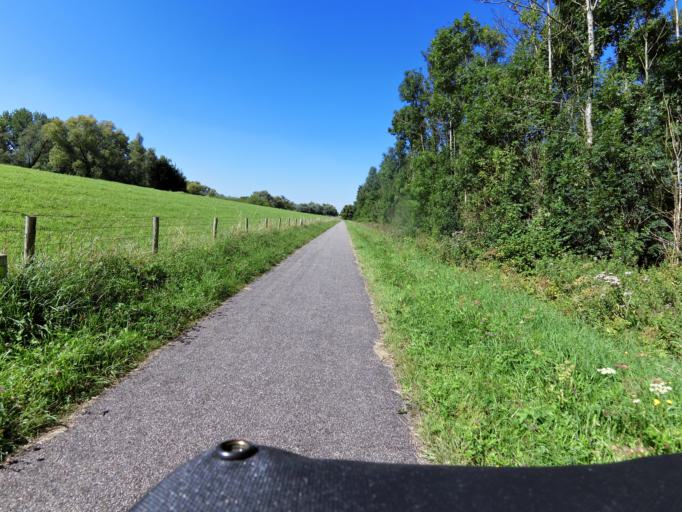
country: NL
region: South Holland
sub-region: Gemeente Dordrecht
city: Dordrecht
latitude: 51.7536
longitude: 4.6889
